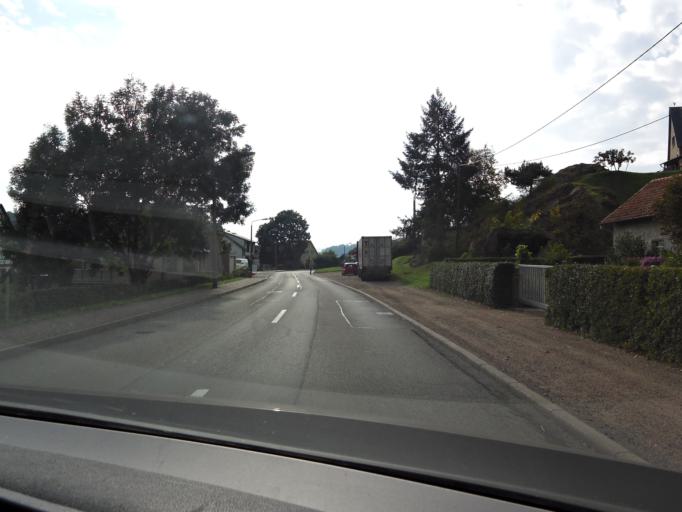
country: DE
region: Thuringia
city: Trusetal
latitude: 50.7806
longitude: 10.4033
